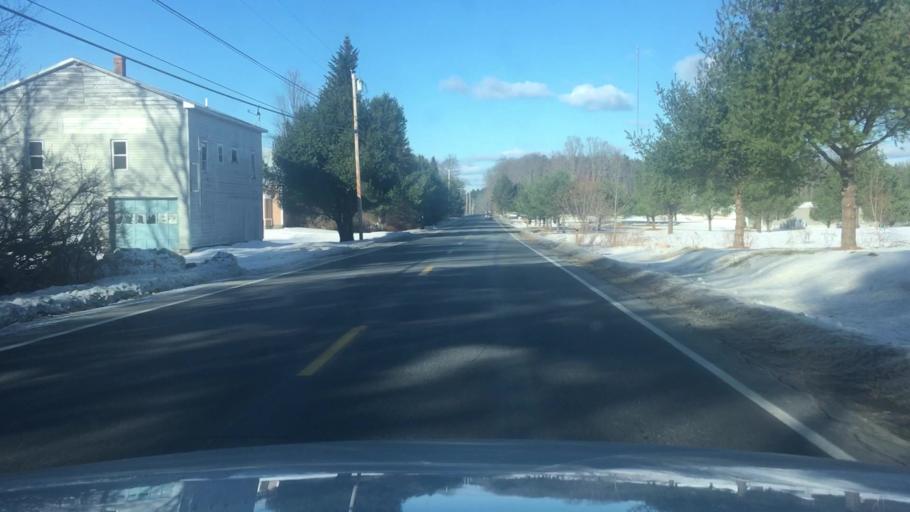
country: US
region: Maine
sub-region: Somerset County
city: Skowhegan
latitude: 44.7406
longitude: -69.6878
